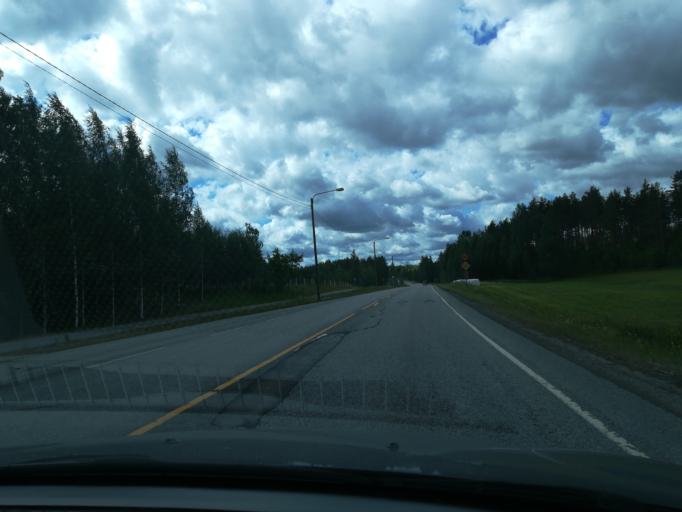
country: FI
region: Southern Savonia
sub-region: Mikkeli
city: Ristiina
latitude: 61.5102
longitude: 27.2399
